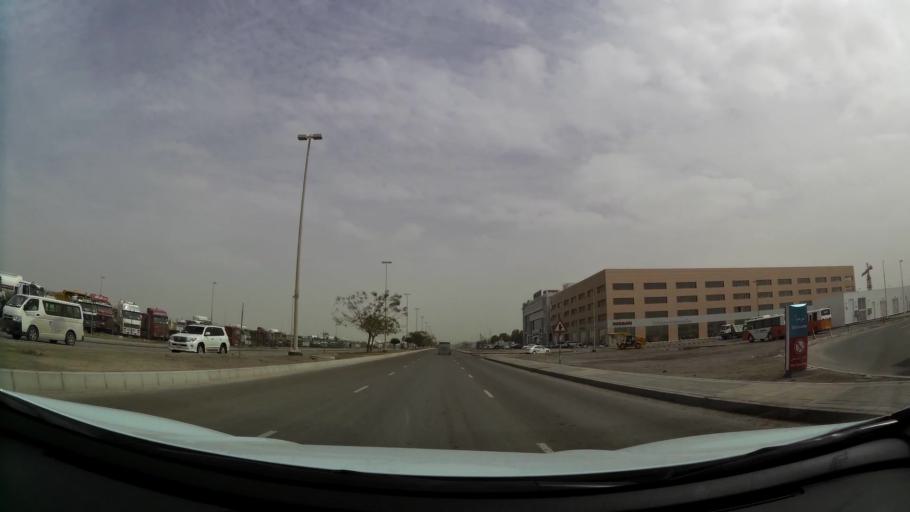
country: AE
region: Abu Dhabi
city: Abu Dhabi
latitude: 24.3582
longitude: 54.4743
